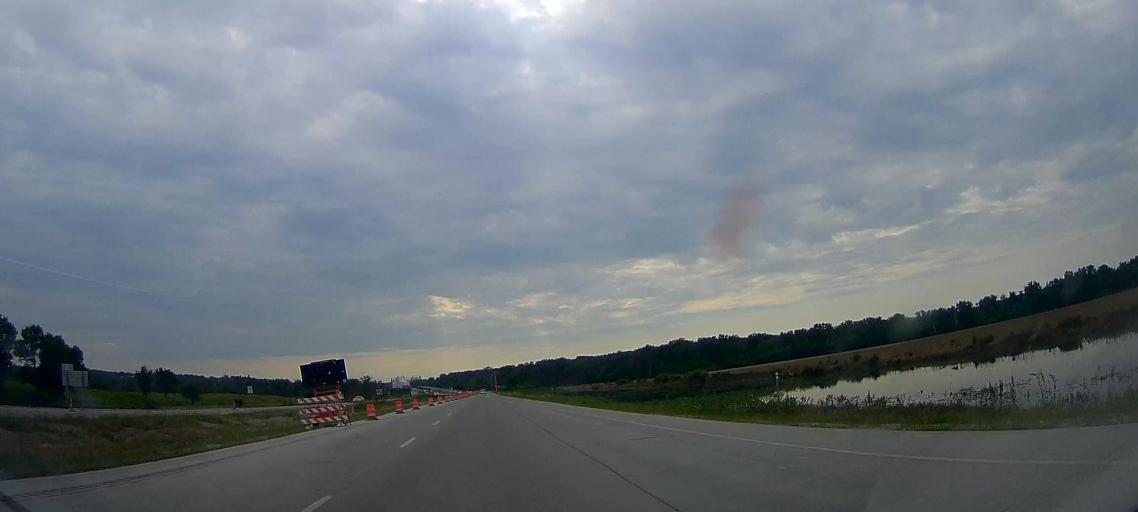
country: US
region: Iowa
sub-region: Pottawattamie County
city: Carter Lake
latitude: 41.3467
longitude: -95.9430
